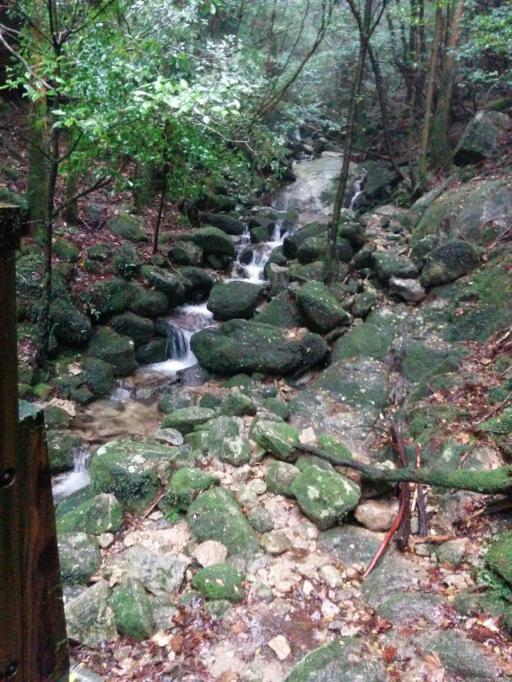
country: JP
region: Kagoshima
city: Nishinoomote
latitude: 30.3538
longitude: 130.5474
